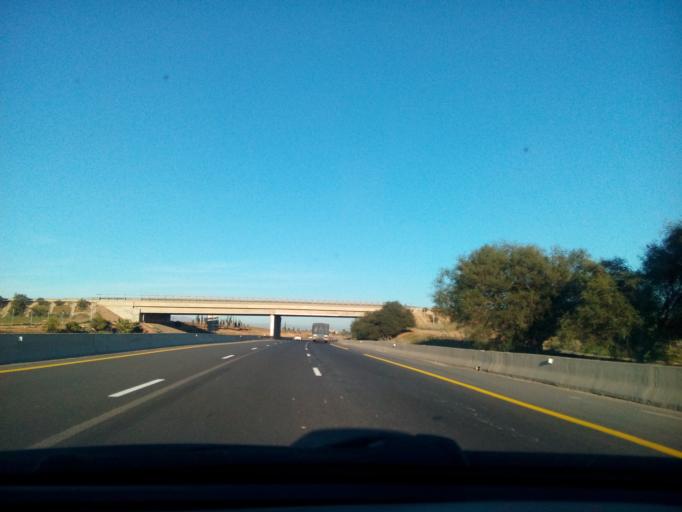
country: DZ
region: Relizane
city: Djidiouia
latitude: 35.8961
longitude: 0.7101
